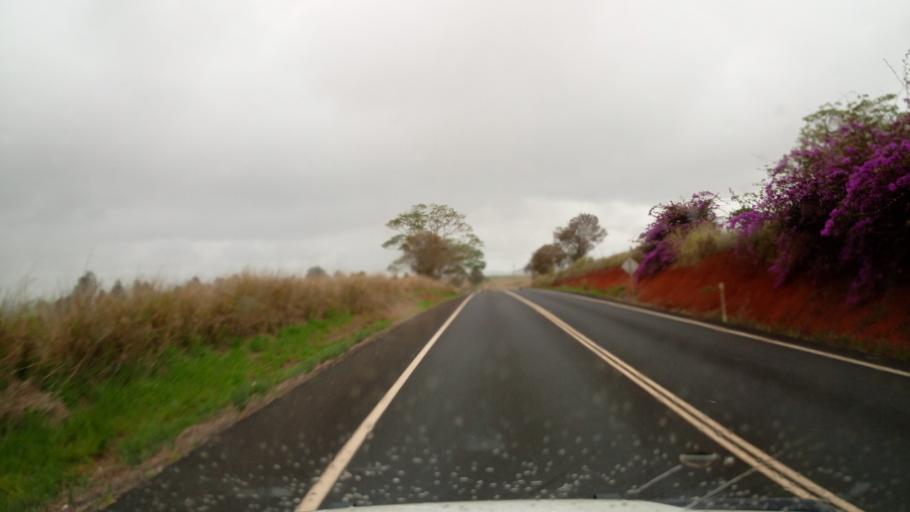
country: AU
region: Queensland
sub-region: Tablelands
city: Atherton
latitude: -17.2814
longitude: 145.6040
